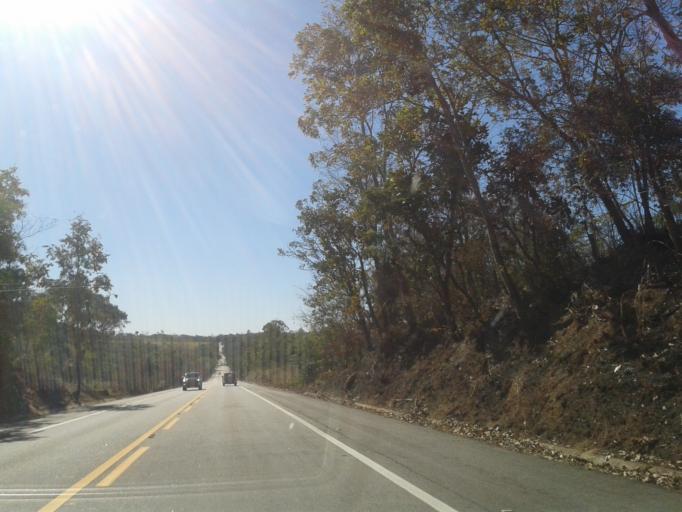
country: BR
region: Goias
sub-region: Itapuranga
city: Itapuranga
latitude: -15.6039
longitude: -50.2522
